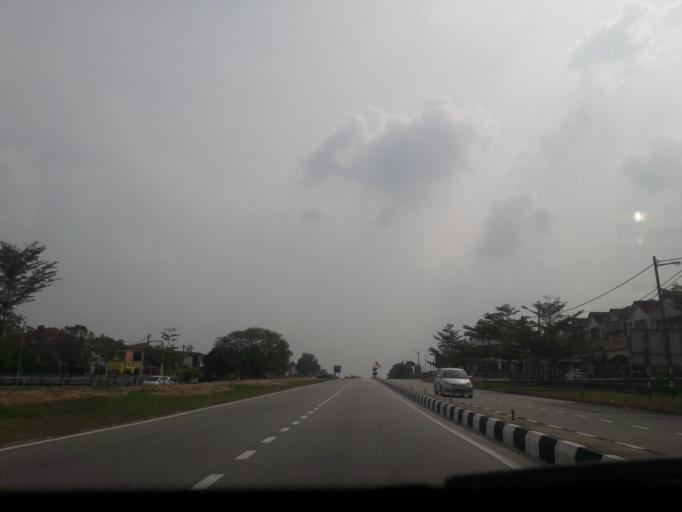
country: MY
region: Kedah
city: Kulim
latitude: 5.3699
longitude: 100.5329
